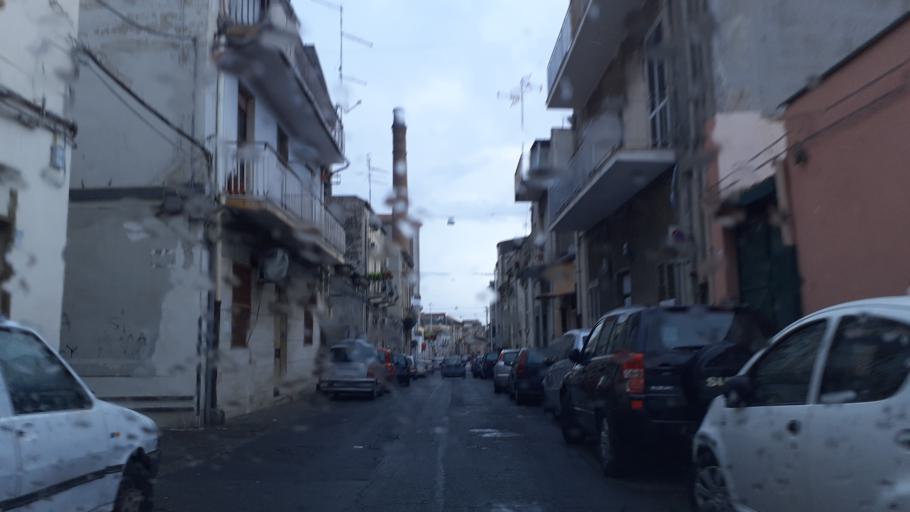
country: IT
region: Sicily
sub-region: Catania
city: Catania
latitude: 37.5049
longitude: 15.0711
